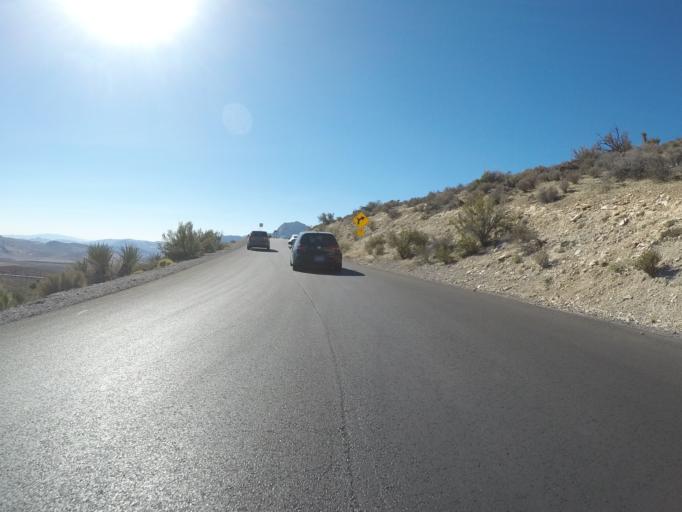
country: US
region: Nevada
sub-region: Clark County
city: Summerlin South
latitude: 36.1718
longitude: -115.4659
